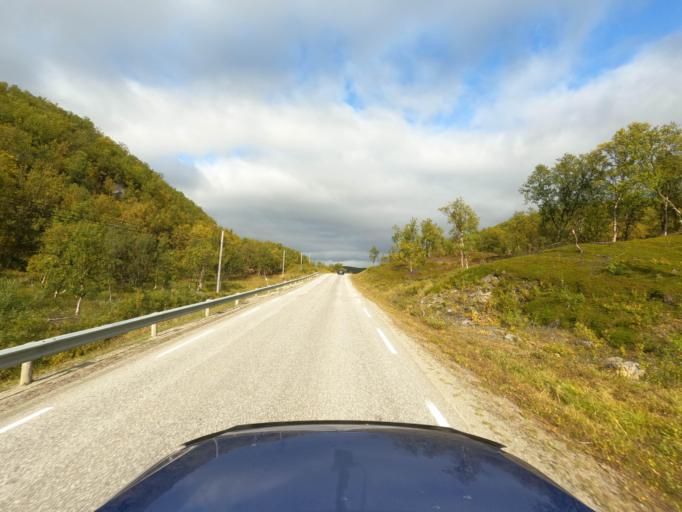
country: NO
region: Finnmark Fylke
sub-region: Porsanger
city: Lakselv
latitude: 70.2809
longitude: 25.0653
